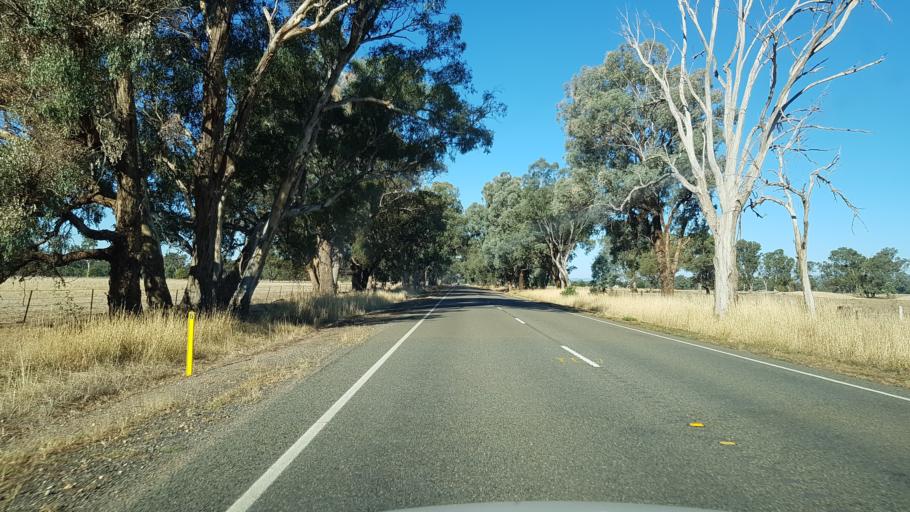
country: AU
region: Victoria
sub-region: Wangaratta
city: Wangaratta
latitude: -36.4369
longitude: 146.3334
